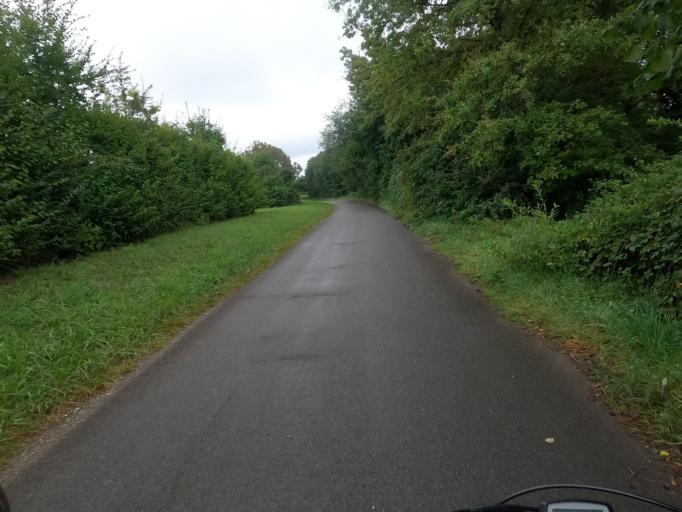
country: DE
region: Baden-Wuerttemberg
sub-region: Freiburg Region
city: Allensbach
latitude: 47.7261
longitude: 9.0405
